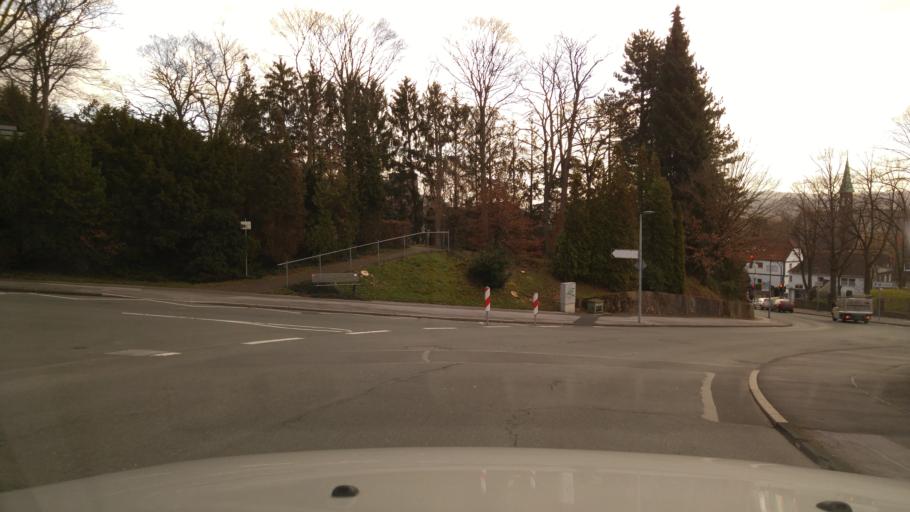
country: DE
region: North Rhine-Westphalia
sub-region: Regierungsbezirk Arnsberg
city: Menden
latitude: 51.4402
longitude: 7.7964
